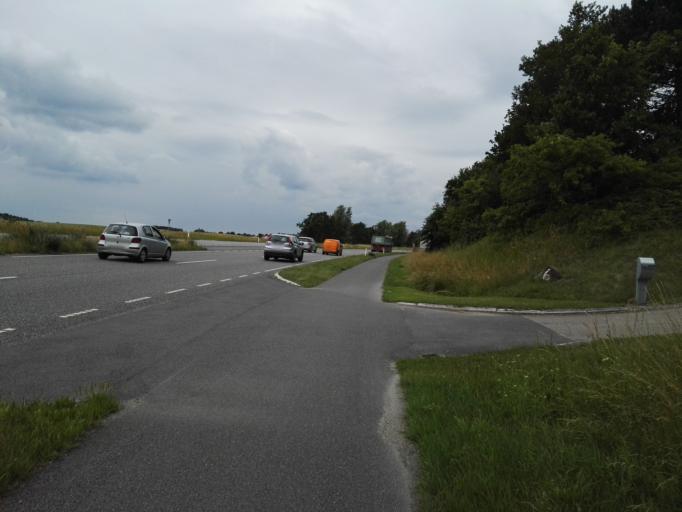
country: DK
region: Capital Region
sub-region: Egedal Kommune
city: Vekso
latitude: 55.7515
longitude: 12.2569
